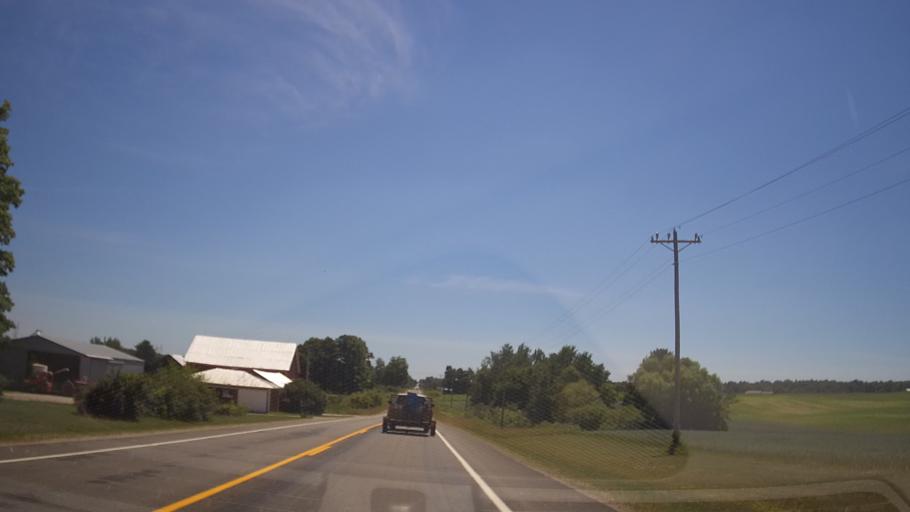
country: US
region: Michigan
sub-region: Grand Traverse County
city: Kingsley
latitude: 44.6065
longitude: -85.6965
